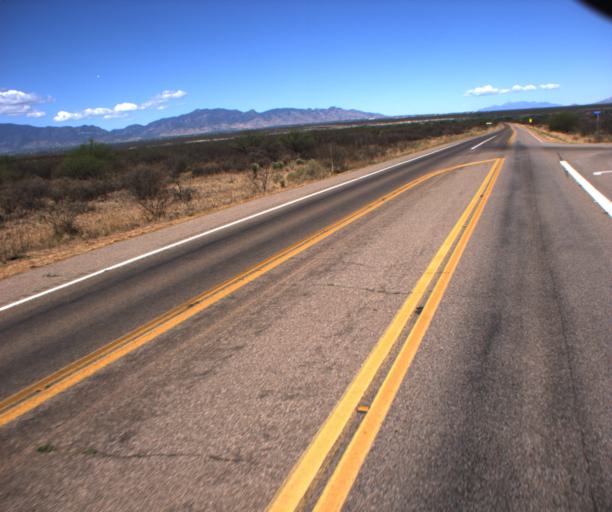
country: US
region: Arizona
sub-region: Cochise County
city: Sierra Vista Southeast
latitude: 31.5514
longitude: -110.1164
